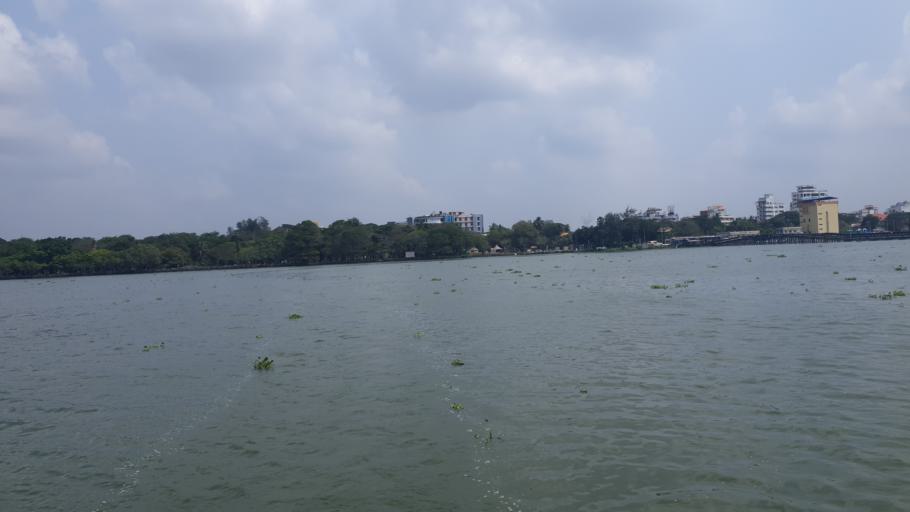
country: IN
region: Kerala
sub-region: Ernakulam
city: Cochin
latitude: 9.9679
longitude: 76.2766
